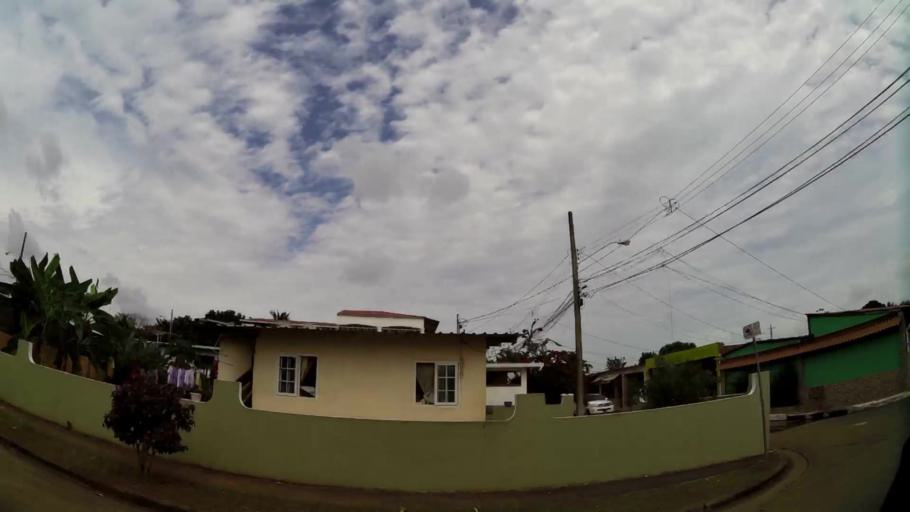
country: PA
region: Panama
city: Tocumen
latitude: 9.0472
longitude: -79.4146
